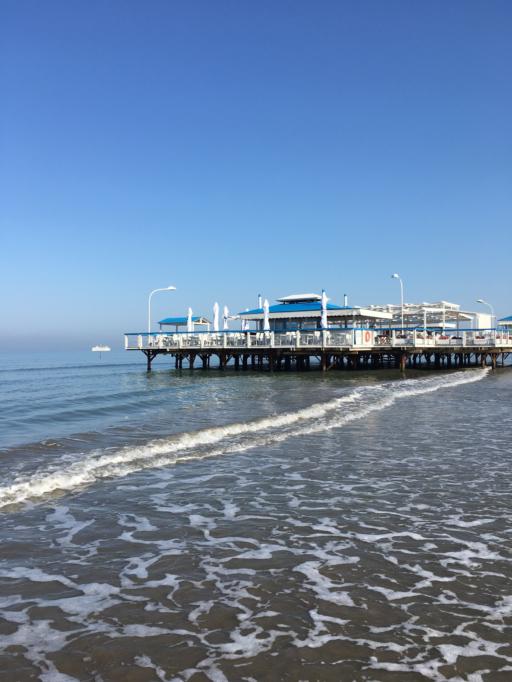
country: AL
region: Tirane
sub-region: Rrethi i Kavajes
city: Golem
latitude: 41.2799
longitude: 19.5123
